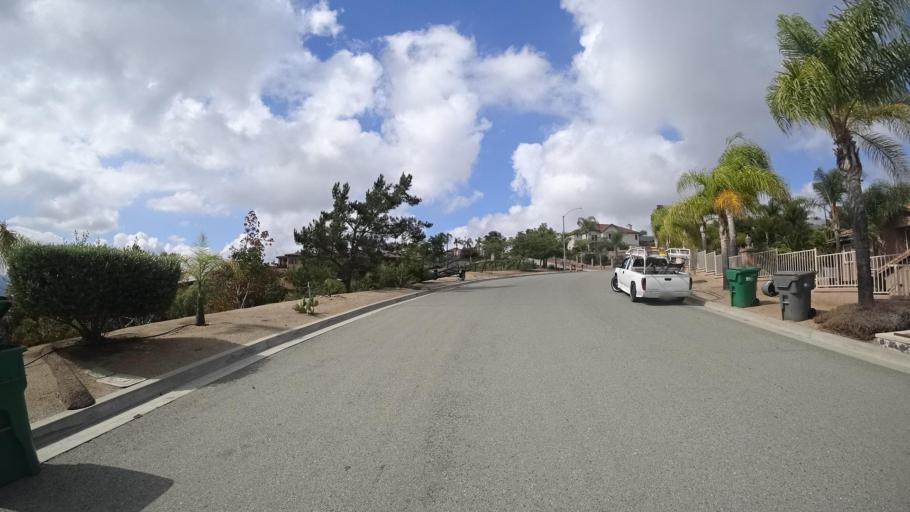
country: US
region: California
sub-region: San Diego County
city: Granite Hills
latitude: 32.7761
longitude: -116.9085
